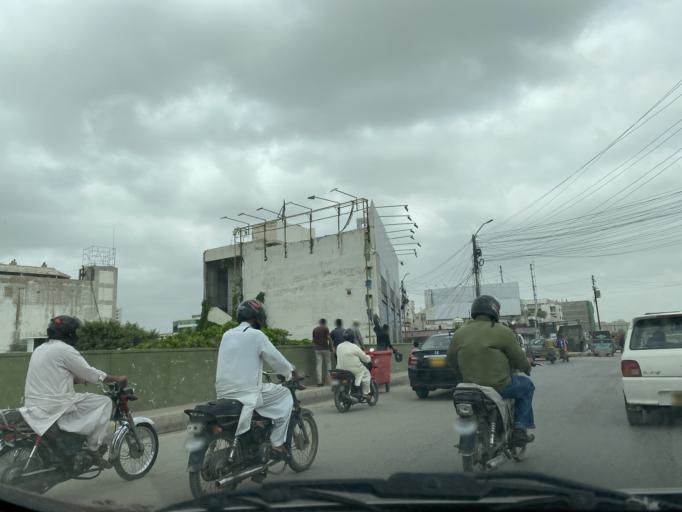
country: PK
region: Sindh
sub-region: Karachi District
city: Karachi
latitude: 24.8666
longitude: 67.0834
